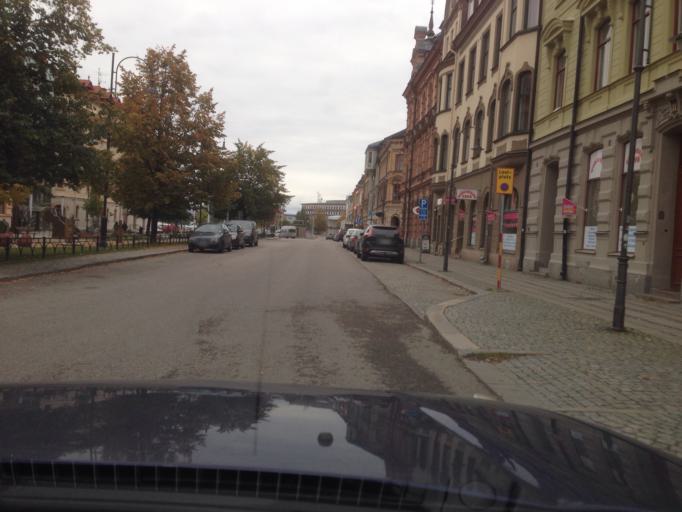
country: SE
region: Vaesternorrland
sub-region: Sundsvalls Kommun
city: Sundsvall
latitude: 62.3916
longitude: 17.3104
